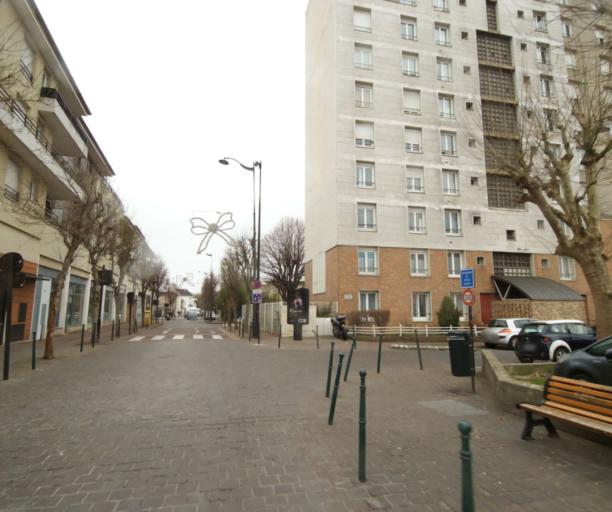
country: FR
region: Ile-de-France
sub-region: Departement des Hauts-de-Seine
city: Rueil-Malmaison
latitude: 48.8864
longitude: 2.1797
